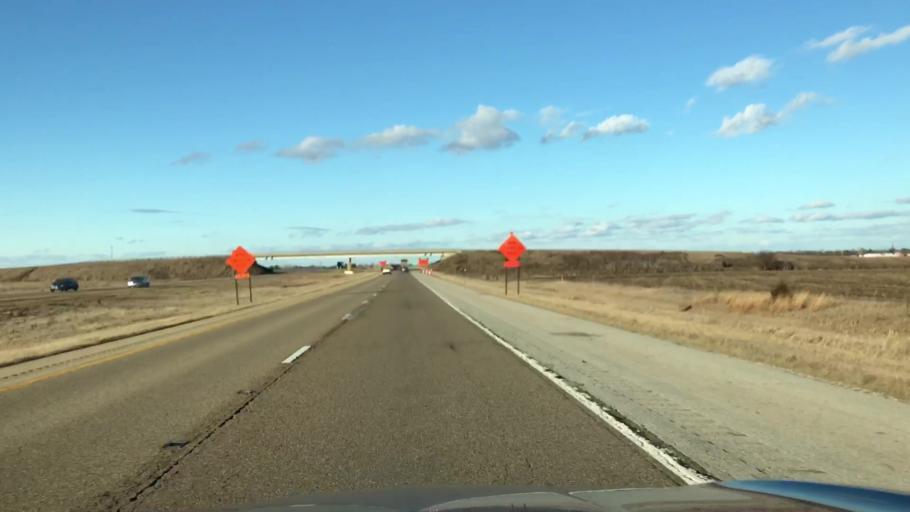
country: US
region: Illinois
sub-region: McLean County
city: Chenoa
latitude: 40.7242
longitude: -88.7370
